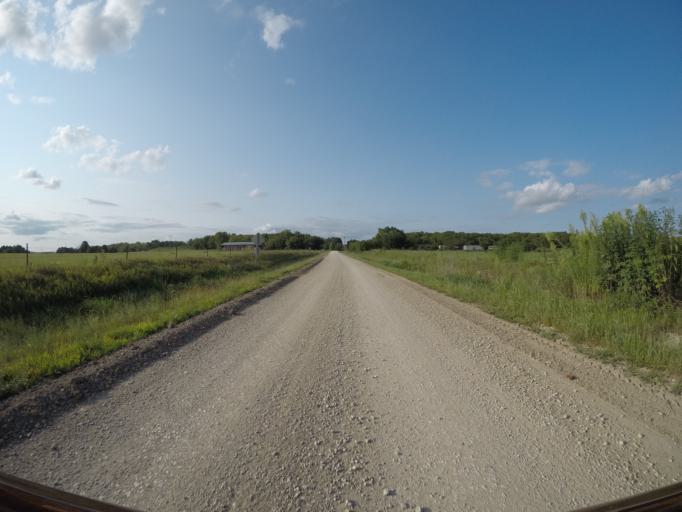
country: US
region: Kansas
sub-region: Wabaunsee County
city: Alma
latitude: 38.9104
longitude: -96.2094
